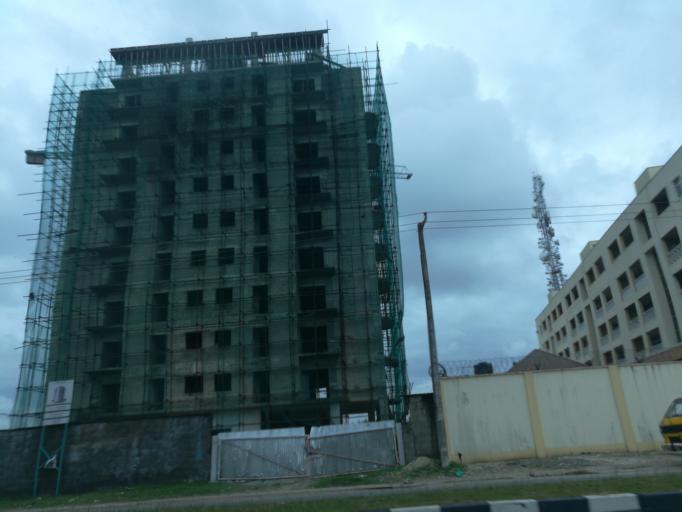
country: NG
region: Lagos
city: Ikoyi
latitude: 6.4477
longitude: 3.4688
